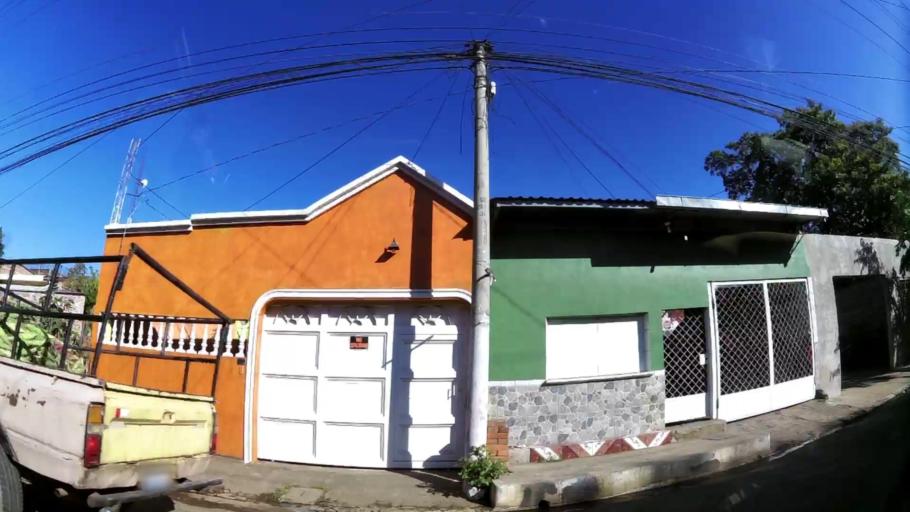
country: SV
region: Sonsonate
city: Sonzacate
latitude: 13.7373
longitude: -89.7131
